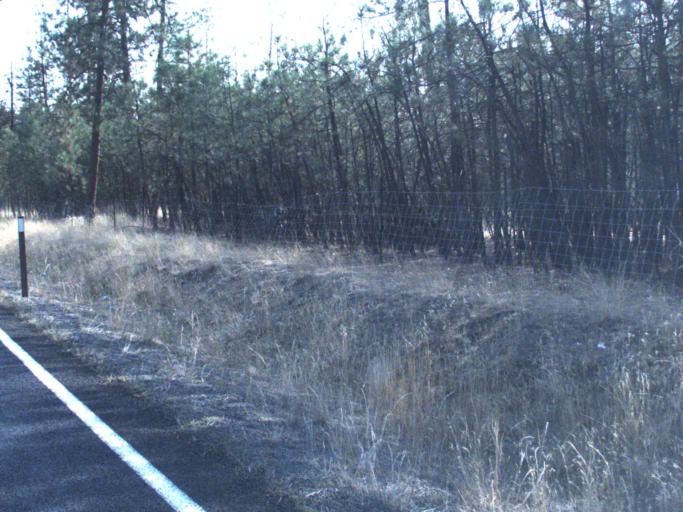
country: US
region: Washington
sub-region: Spokane County
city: Fairchild Air Force Base
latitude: 47.8467
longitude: -117.7279
